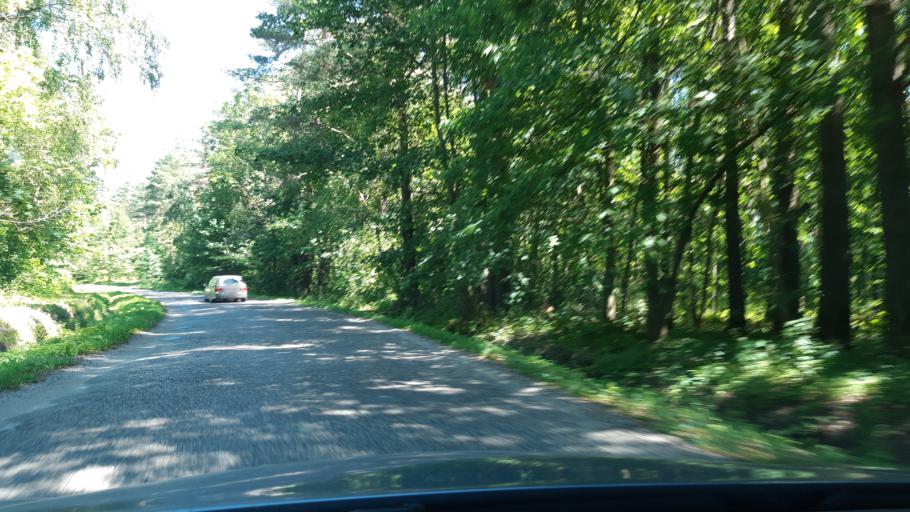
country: PL
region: Warmian-Masurian Voivodeship
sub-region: Powiat gizycki
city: Gizycko
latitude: 53.9457
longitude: 21.7492
